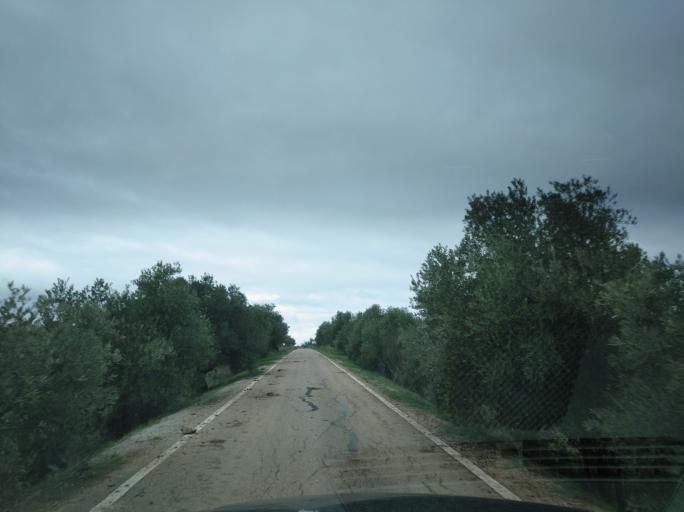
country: PT
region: Portalegre
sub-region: Campo Maior
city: Campo Maior
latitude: 38.9854
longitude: -7.0389
